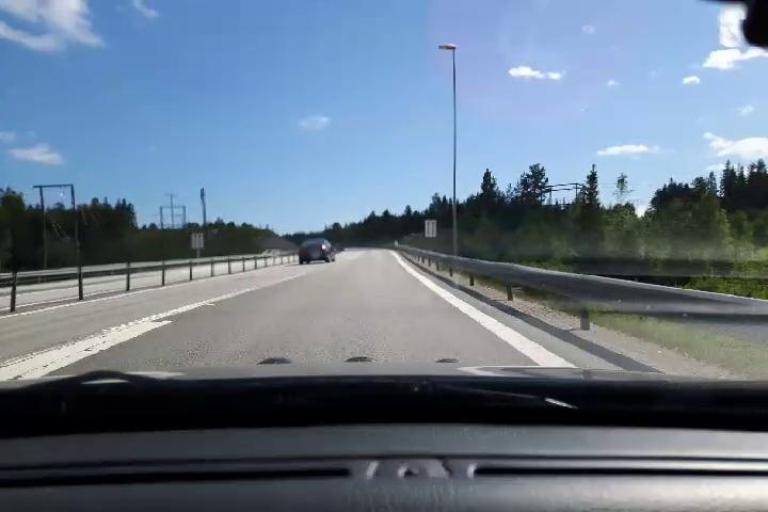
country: SE
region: Gaevleborg
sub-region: Hudiksvalls Kommun
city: Hudiksvall
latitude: 61.7120
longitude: 17.0483
